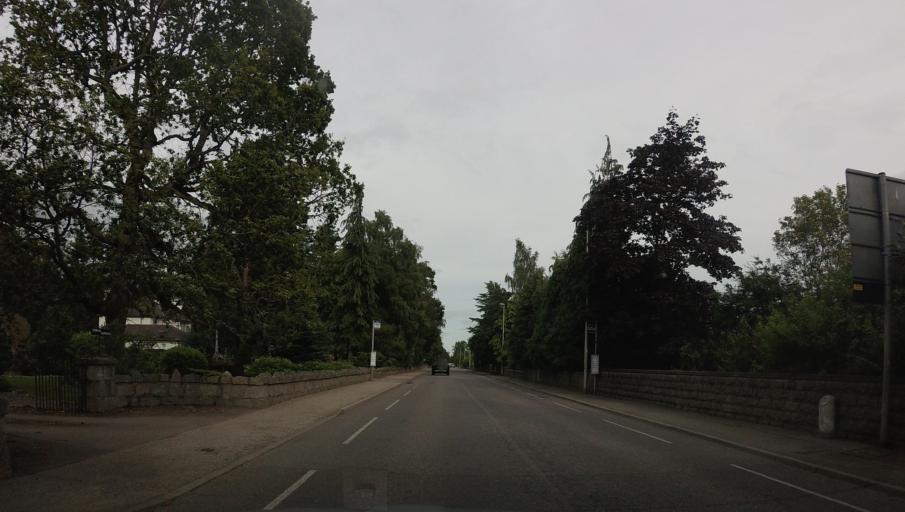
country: GB
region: Scotland
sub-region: Aberdeenshire
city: Aboyne
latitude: 57.0758
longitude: -2.7909
